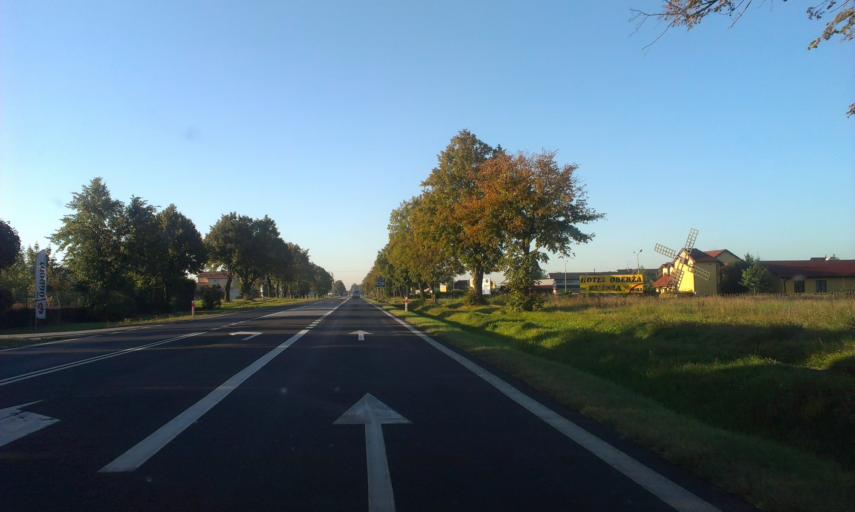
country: PL
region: Kujawsko-Pomorskie
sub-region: Powiat torunski
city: Lysomice
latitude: 53.0959
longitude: 18.6217
